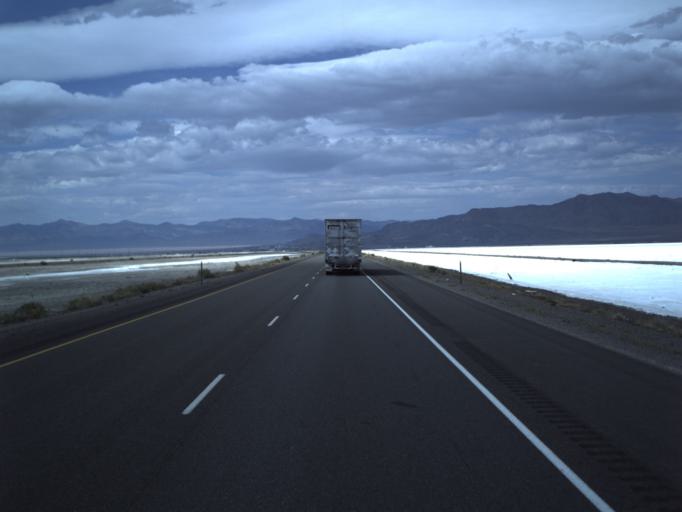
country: US
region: Utah
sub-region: Tooele County
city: Wendover
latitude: 40.7406
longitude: -113.9137
